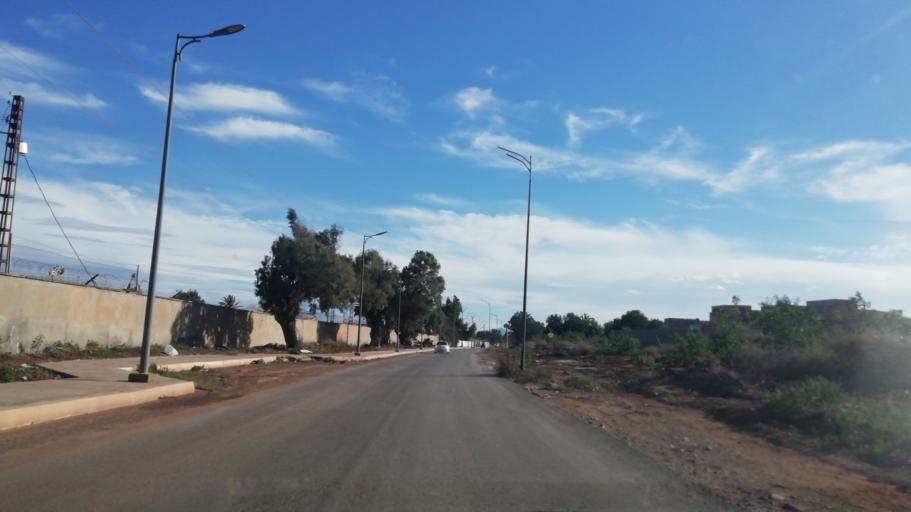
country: DZ
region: Oran
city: Es Senia
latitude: 35.6210
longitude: -0.5871
